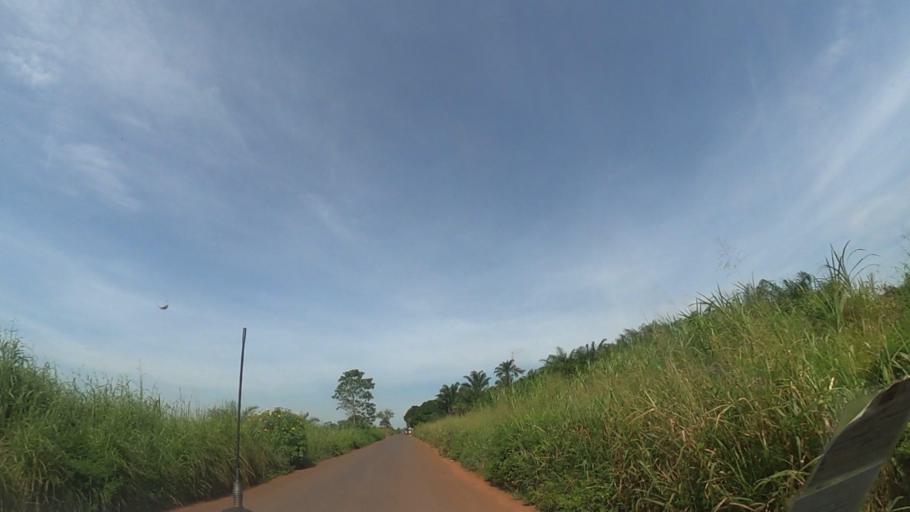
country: CF
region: Ombella-Mpoko
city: Bimbo
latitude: 4.3136
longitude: 18.4726
